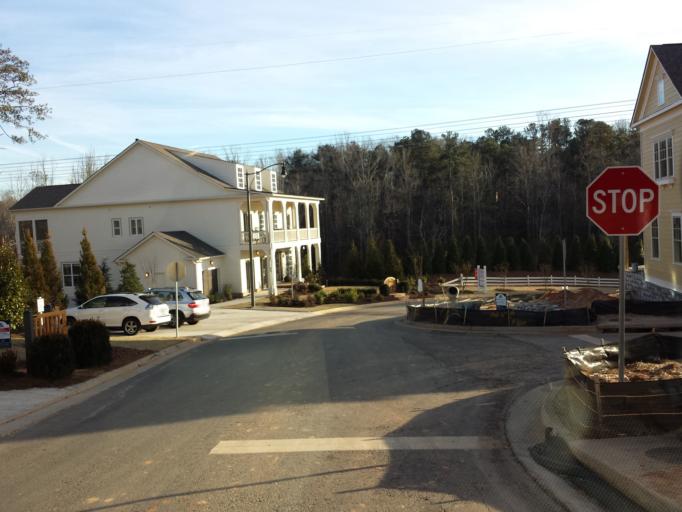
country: US
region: Georgia
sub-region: Cobb County
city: Marietta
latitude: 33.9928
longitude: -84.4736
